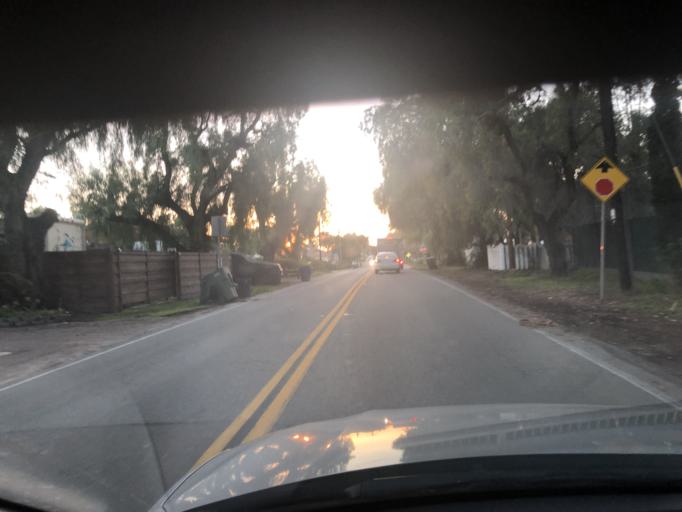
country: US
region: California
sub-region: San Diego County
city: Chula Vista
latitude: 32.6416
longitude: -117.0654
